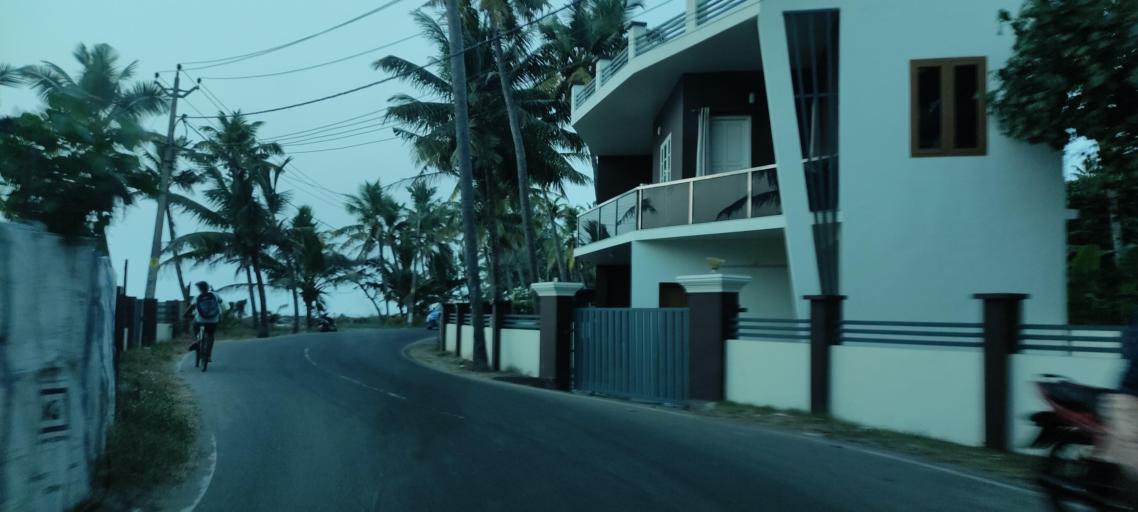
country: IN
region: Kerala
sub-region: Alappuzha
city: Kayankulam
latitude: 9.1249
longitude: 76.4684
